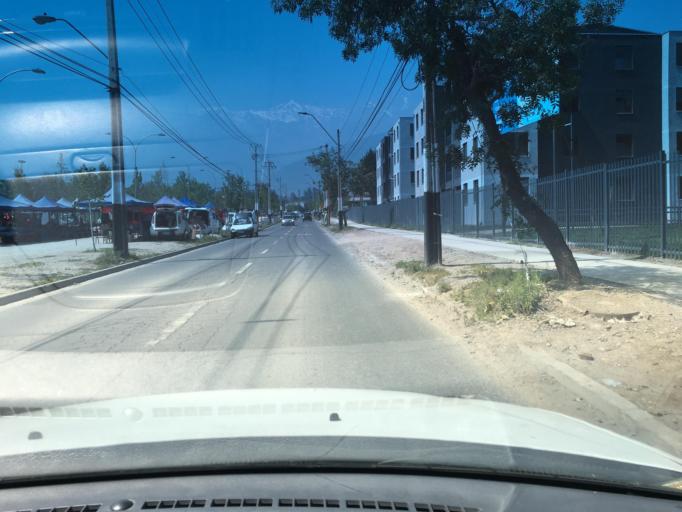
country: CL
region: Santiago Metropolitan
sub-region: Provincia de Santiago
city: Villa Presidente Frei, Nunoa, Santiago, Chile
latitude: -33.5171
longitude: -70.5544
